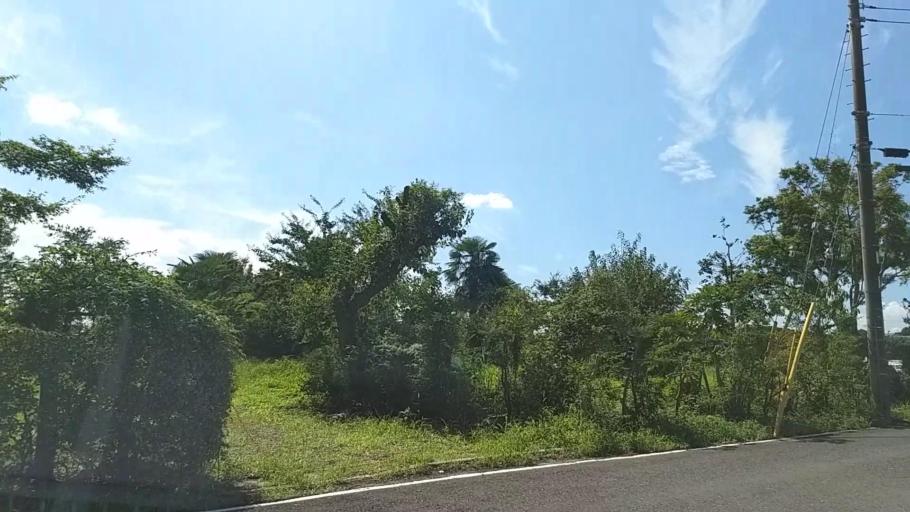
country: JP
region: Tokyo
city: Chofugaoka
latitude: 35.5593
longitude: 139.5681
